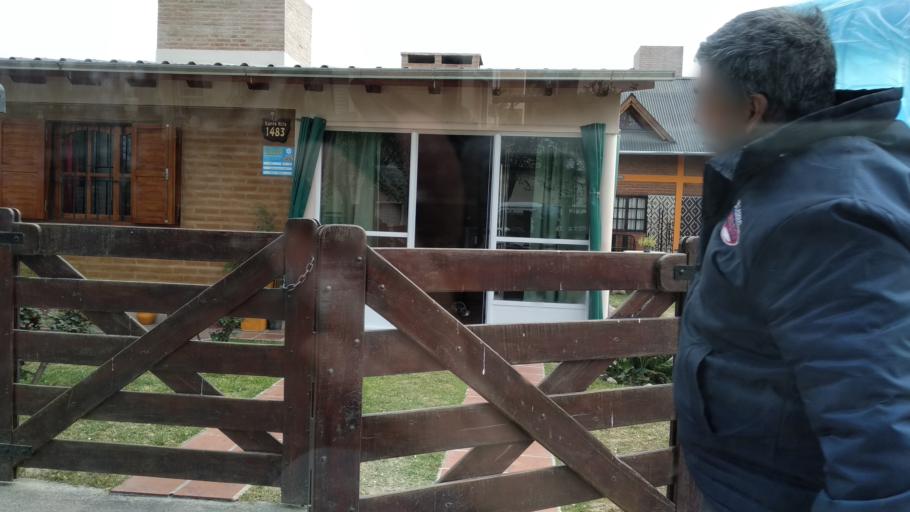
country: AR
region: Cordoba
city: Mina Clavero
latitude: -31.7323
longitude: -65.0149
